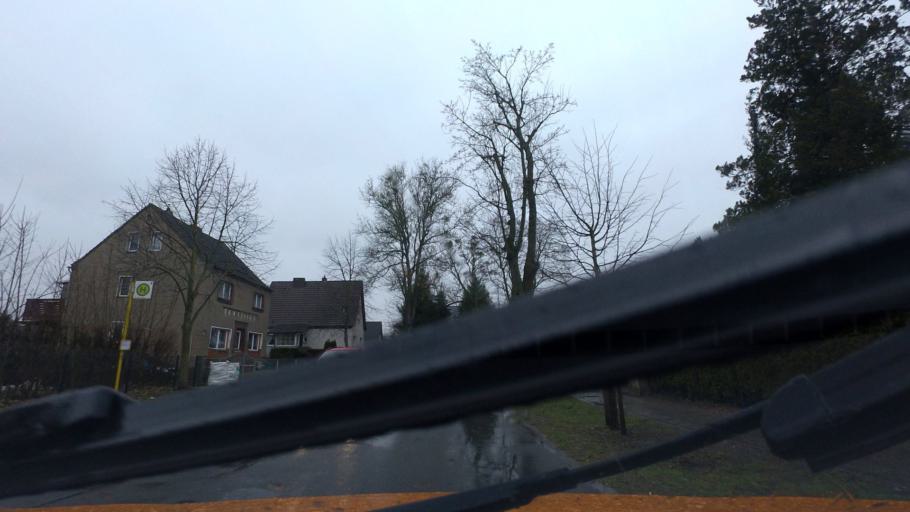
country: DE
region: Brandenburg
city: Brieselang
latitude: 52.5861
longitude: 13.0038
